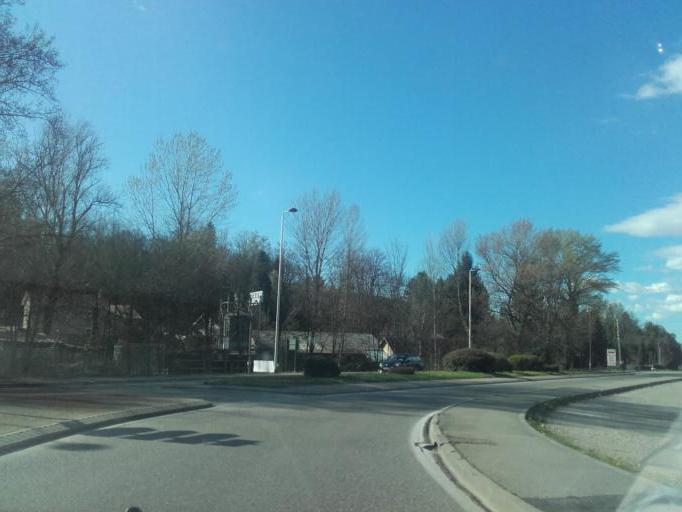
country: FR
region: Rhone-Alpes
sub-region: Departement de l'Isere
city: Nivolas-Vermelle
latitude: 45.5628
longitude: 5.3039
